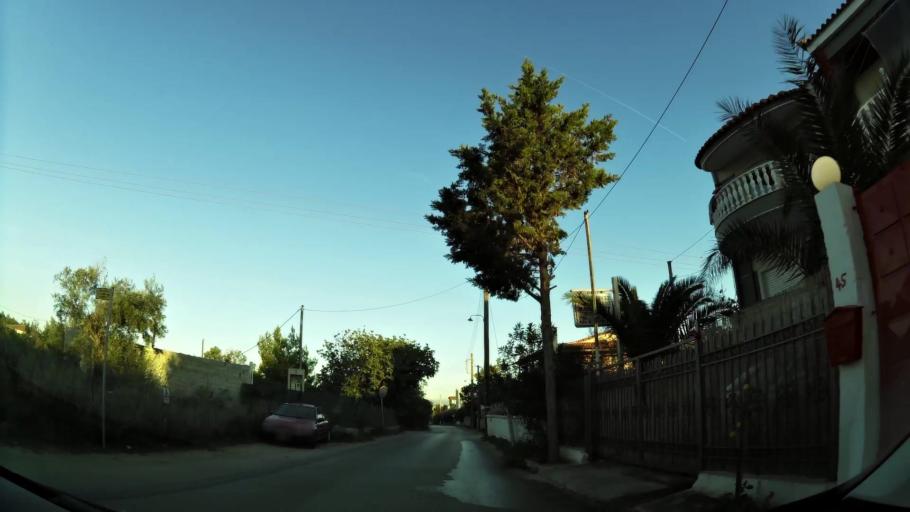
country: GR
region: Attica
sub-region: Nomarchia Anatolikis Attikis
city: Rafina
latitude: 37.9997
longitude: 24.0124
